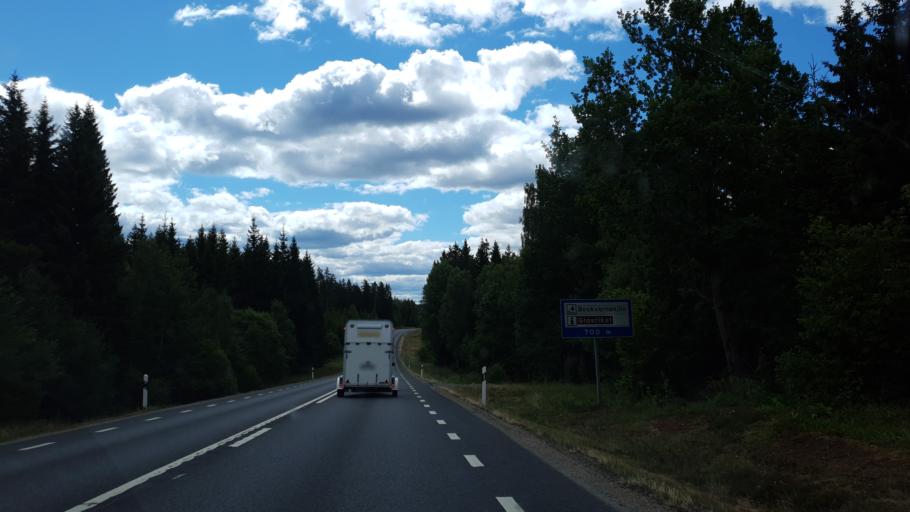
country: SE
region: Joenkoeping
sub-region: Vetlanda Kommun
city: Vetlanda
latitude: 57.2439
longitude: 15.1406
